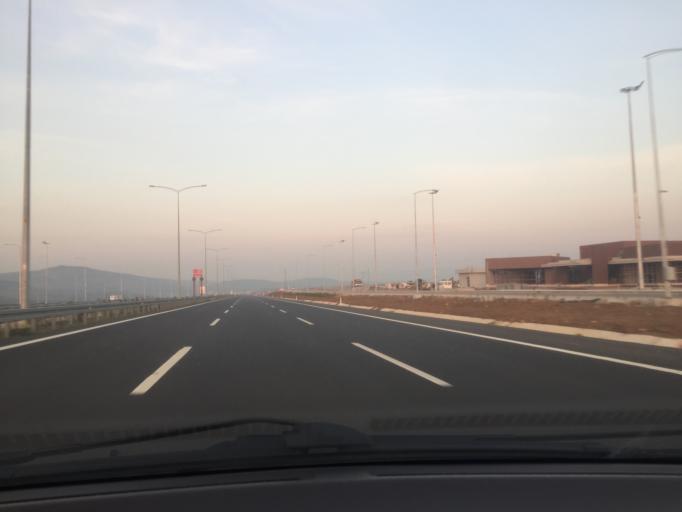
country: TR
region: Bursa
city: Mahmudiye
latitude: 40.2728
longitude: 28.6016
